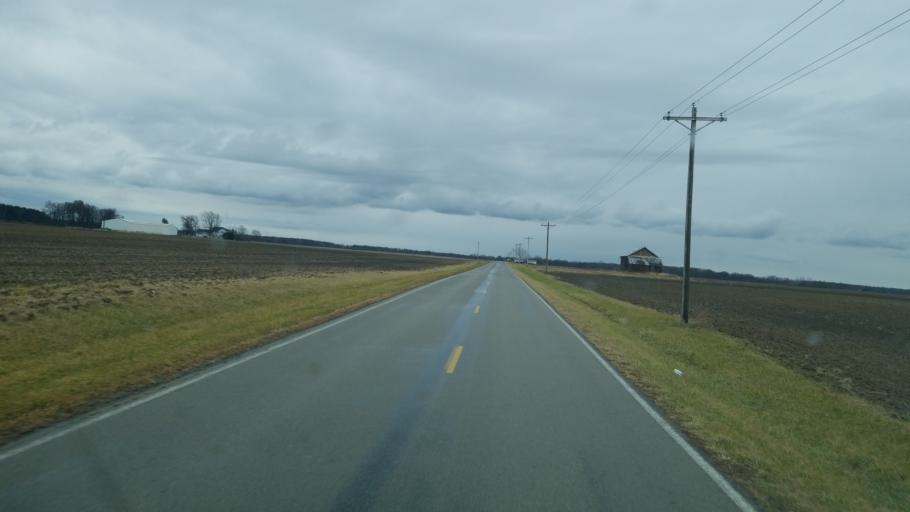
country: US
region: Ohio
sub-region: Hardin County
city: Forest
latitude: 40.7507
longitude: -83.4198
